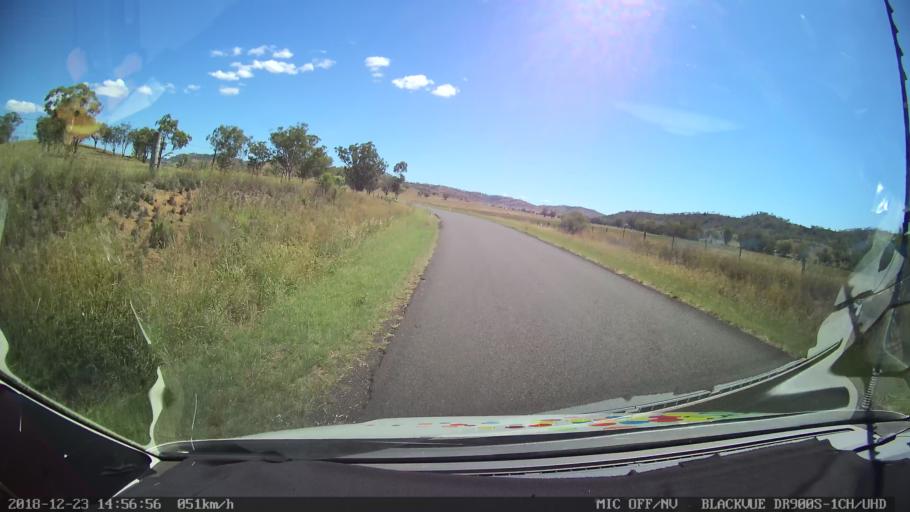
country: AU
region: New South Wales
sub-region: Tamworth Municipality
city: Manilla
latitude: -30.7058
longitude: 150.8288
